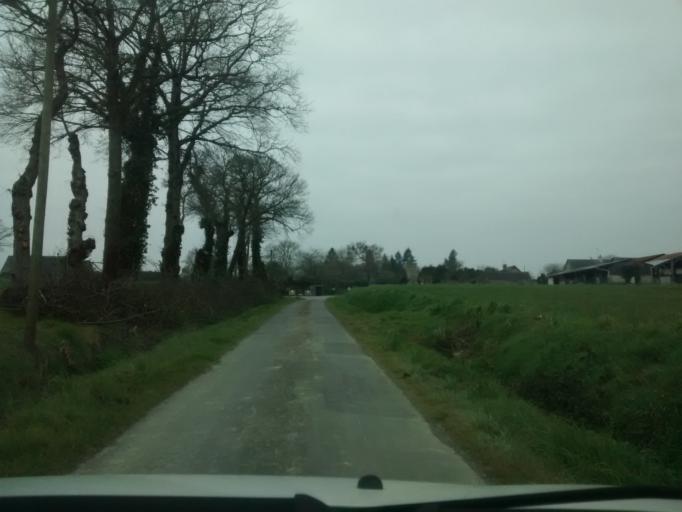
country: FR
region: Brittany
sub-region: Departement d'Ille-et-Vilaine
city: Bazouges-la-Perouse
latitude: 48.3945
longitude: -1.5489
